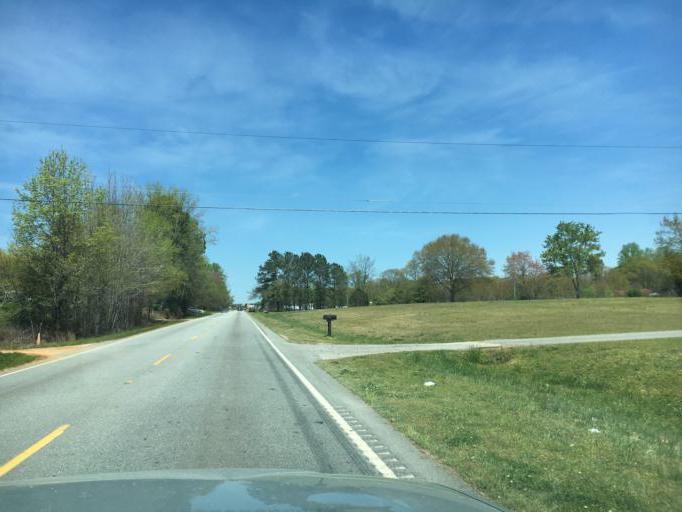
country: US
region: South Carolina
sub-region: Anderson County
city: Williamston
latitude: 34.6590
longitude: -82.5182
